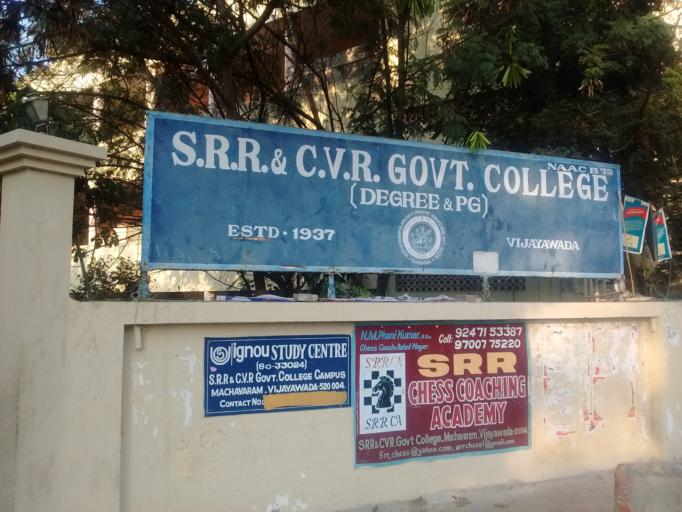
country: IN
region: Andhra Pradesh
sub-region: Krishna
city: Vijayawada
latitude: 16.5189
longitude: 80.6492
